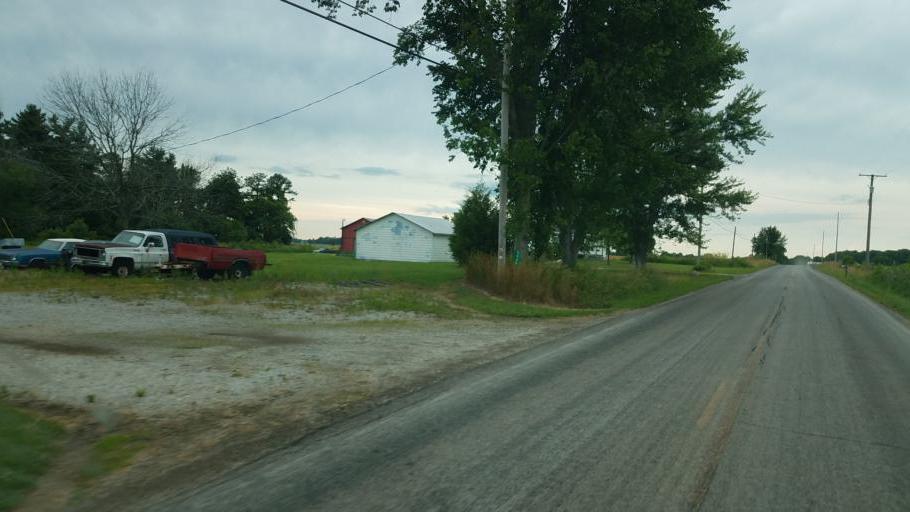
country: US
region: Ohio
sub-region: Huron County
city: Greenwich
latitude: 40.9233
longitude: -82.4439
